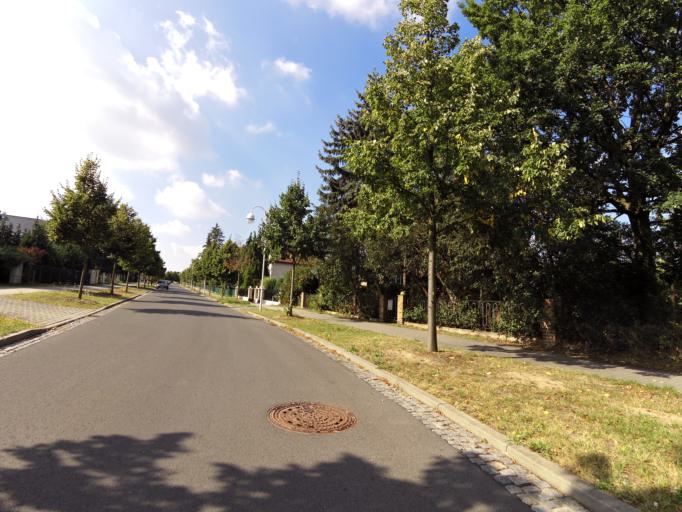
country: DE
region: Berlin
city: Lichtenrade
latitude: 52.3618
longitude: 13.4266
